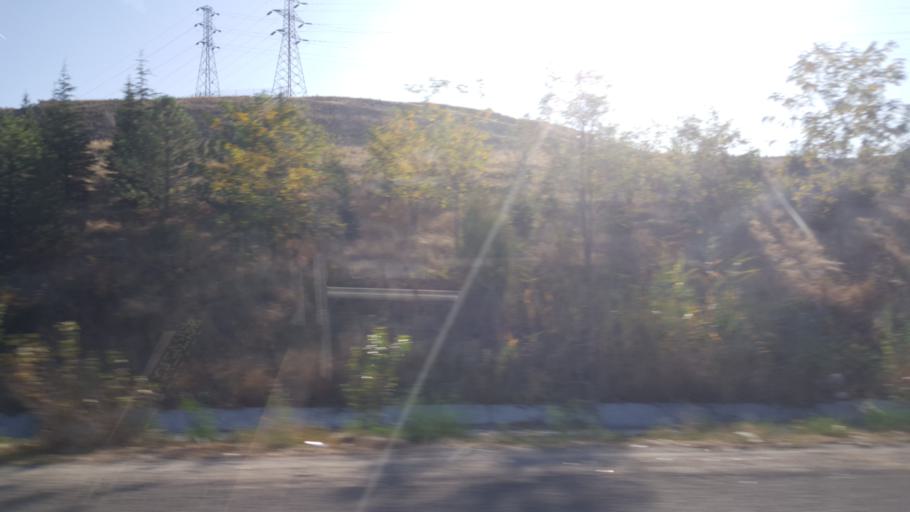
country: TR
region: Ankara
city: Mamak
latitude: 39.8864
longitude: 32.9543
